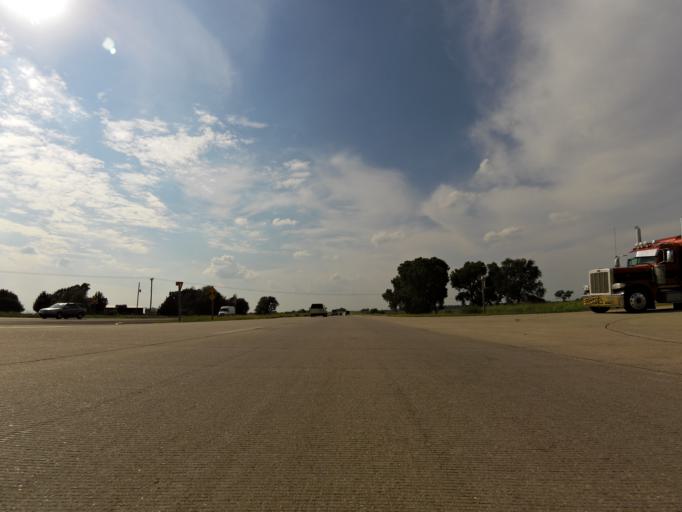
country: US
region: Kansas
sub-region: Sedgwick County
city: Colwich
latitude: 37.8550
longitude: -97.6092
